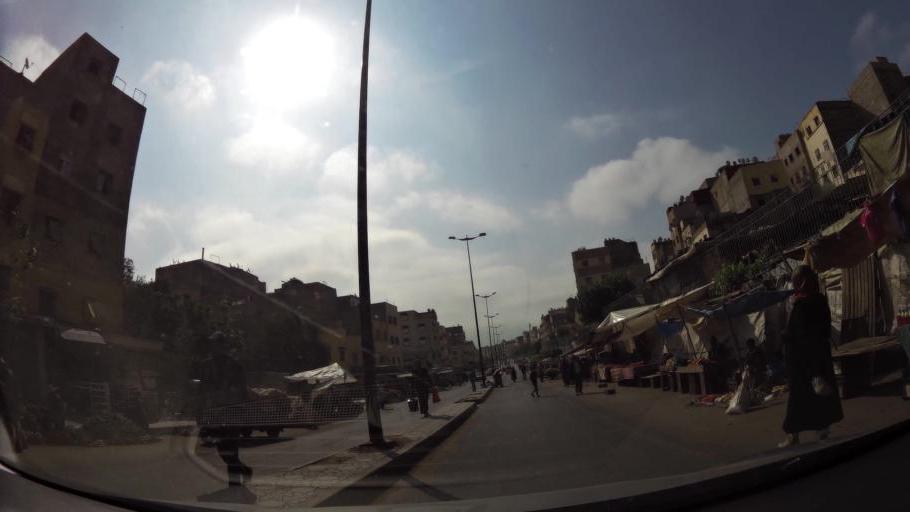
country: MA
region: Fes-Boulemane
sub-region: Fes
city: Fes
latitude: 34.0665
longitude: -5.0055
